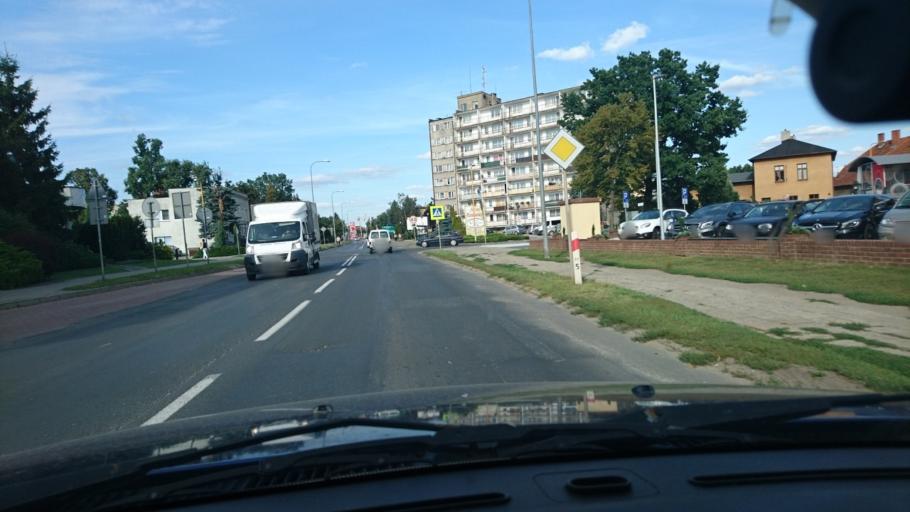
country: PL
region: Greater Poland Voivodeship
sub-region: Powiat krotoszynski
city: Krotoszyn
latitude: 51.6995
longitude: 17.4358
